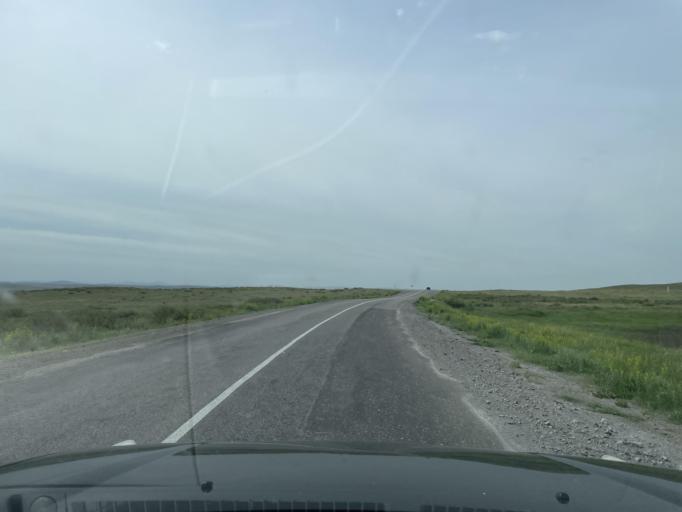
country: KZ
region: Qaraghandy
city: Abay
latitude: 49.4520
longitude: 72.9231
